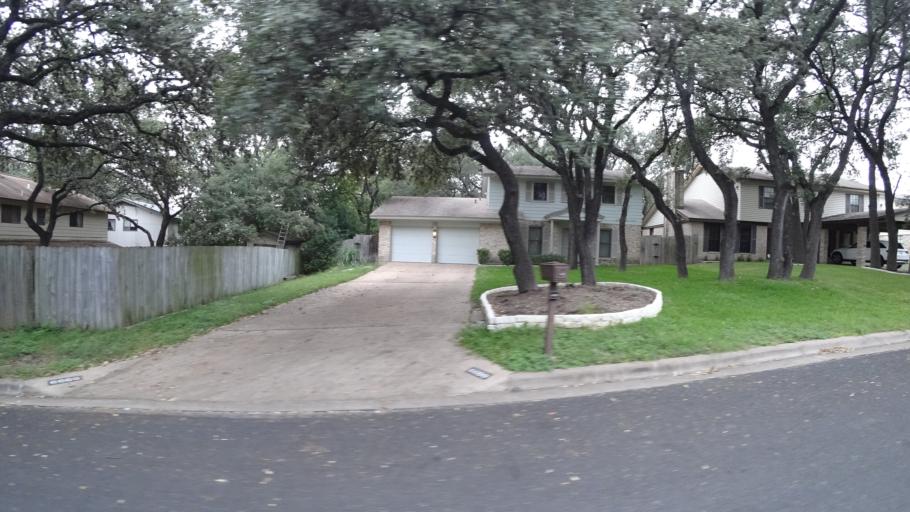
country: US
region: Texas
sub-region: Travis County
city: Onion Creek
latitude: 30.1957
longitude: -97.7821
